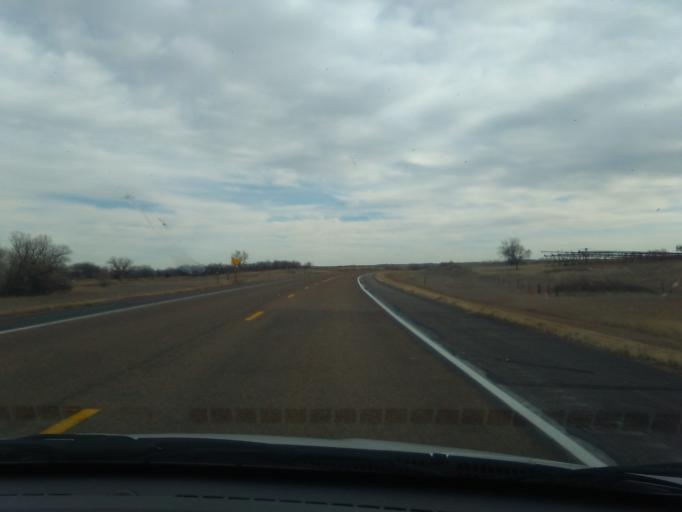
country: US
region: Colorado
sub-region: Yuma County
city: Wray
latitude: 40.0347
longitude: -101.9735
